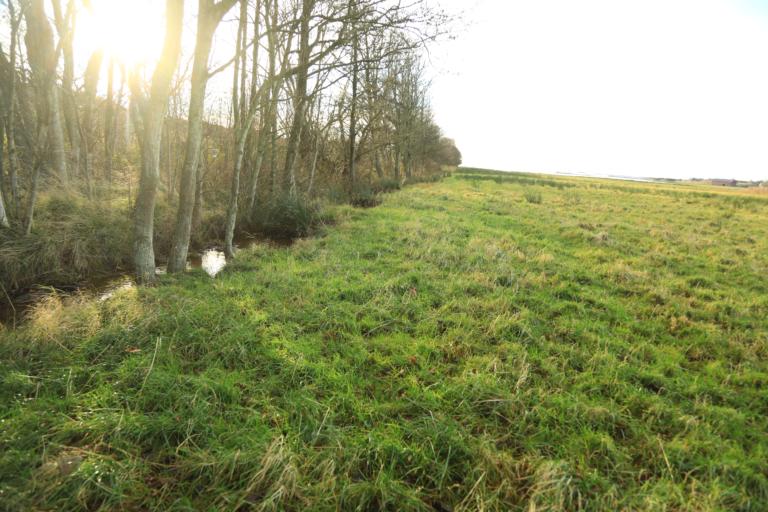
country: SE
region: Halland
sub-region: Varbergs Kommun
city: Varberg
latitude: 57.1637
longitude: 12.2360
